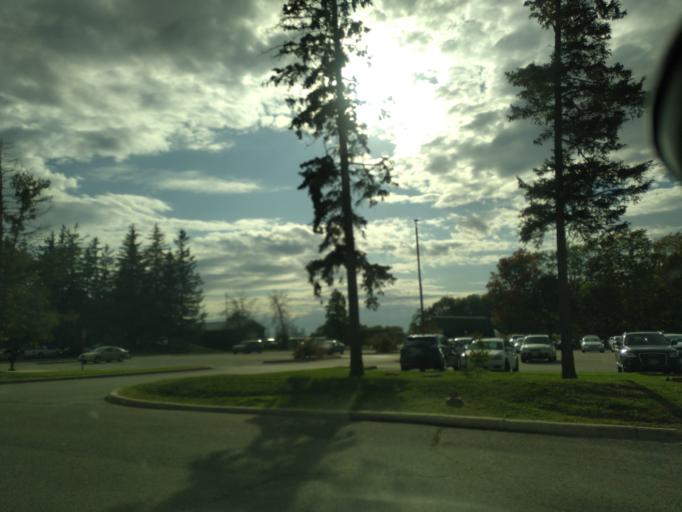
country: CA
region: Ontario
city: Newmarket
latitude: 43.9654
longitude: -79.4616
